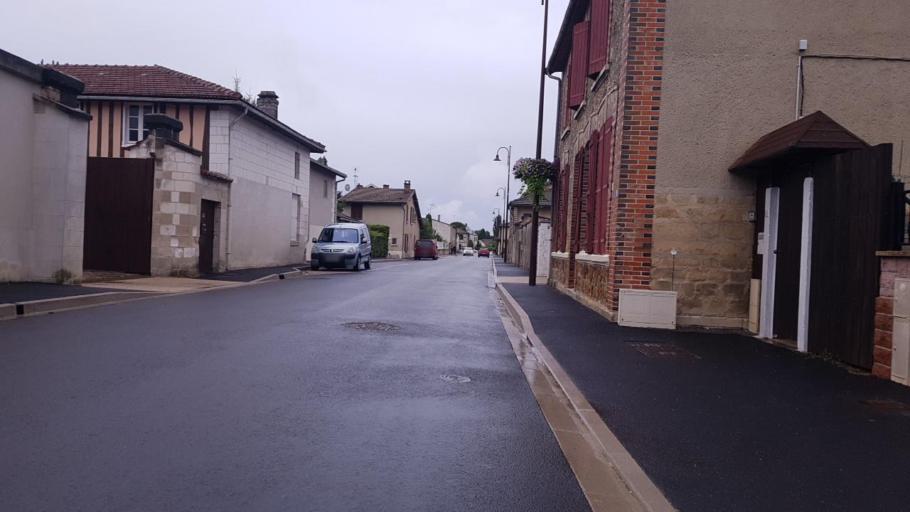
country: FR
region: Champagne-Ardenne
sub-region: Departement de la Marne
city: Sarry
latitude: 48.9194
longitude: 4.4043
